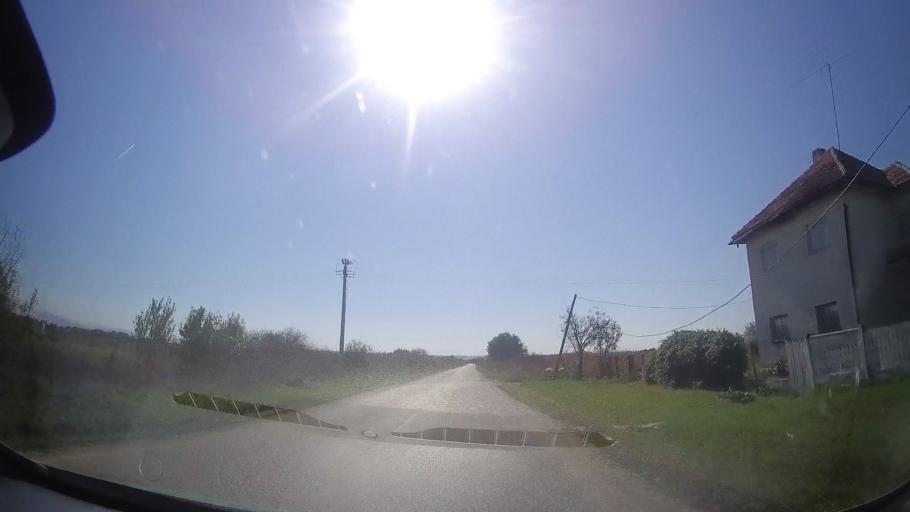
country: RO
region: Timis
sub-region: Comuna Bethausen
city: Bethausen
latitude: 45.8261
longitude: 21.9596
